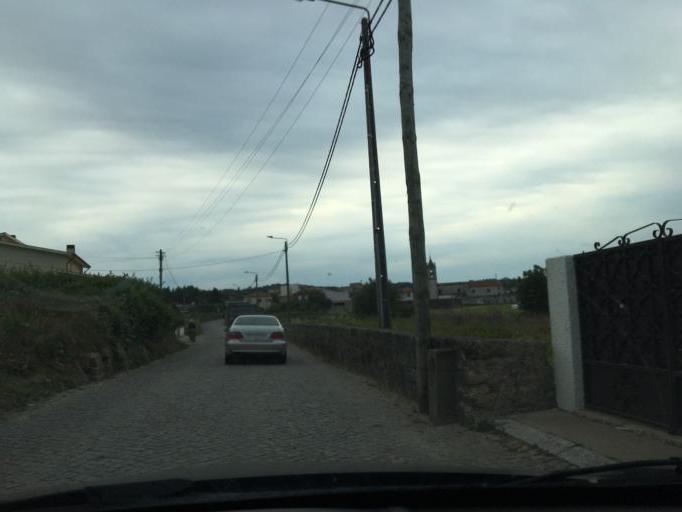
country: PT
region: Porto
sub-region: Maia
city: Anta
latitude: 41.2740
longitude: -8.6179
